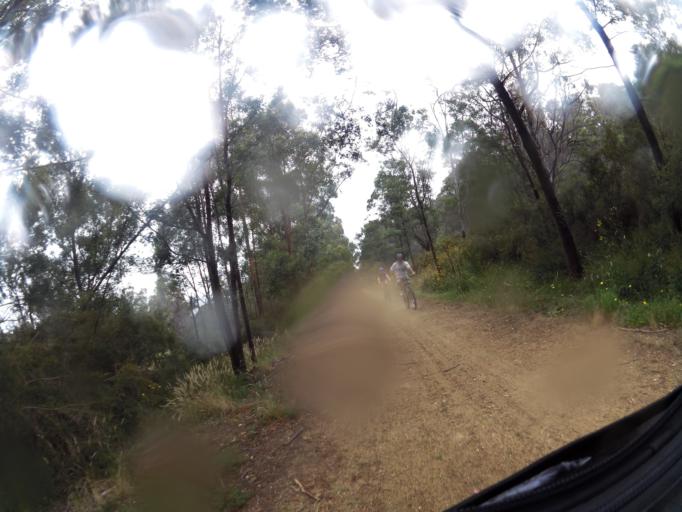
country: AU
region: Victoria
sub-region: East Gippsland
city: Lakes Entrance
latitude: -37.7513
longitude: 147.8121
